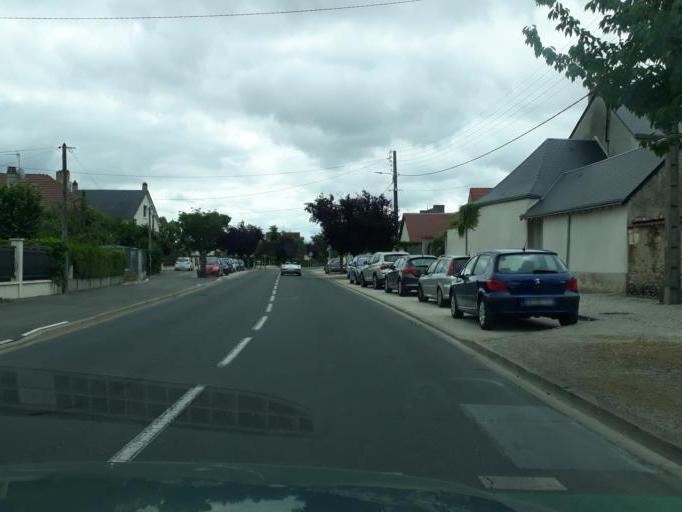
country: FR
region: Centre
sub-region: Departement du Loiret
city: Saint-Jean-le-Blanc
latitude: 47.8760
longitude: 1.9343
